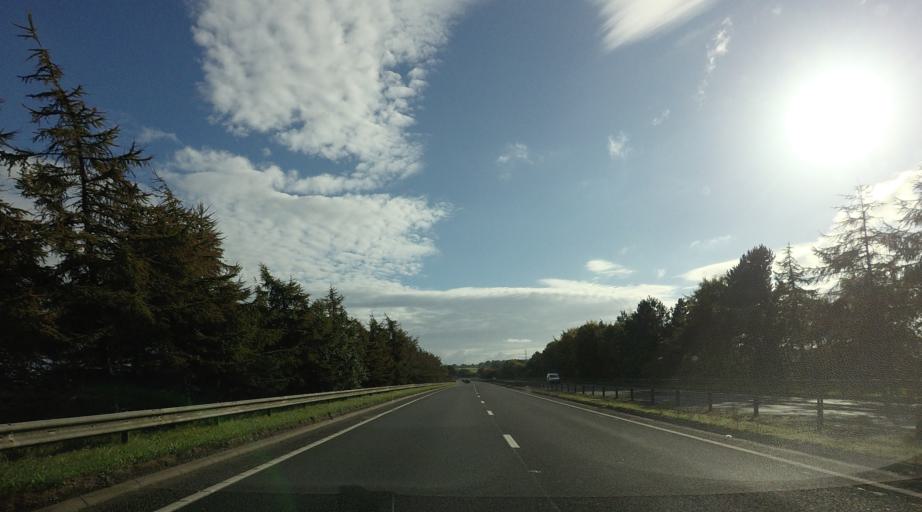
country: GB
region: Scotland
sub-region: Fife
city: Thornton
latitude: 56.1611
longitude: -3.1370
